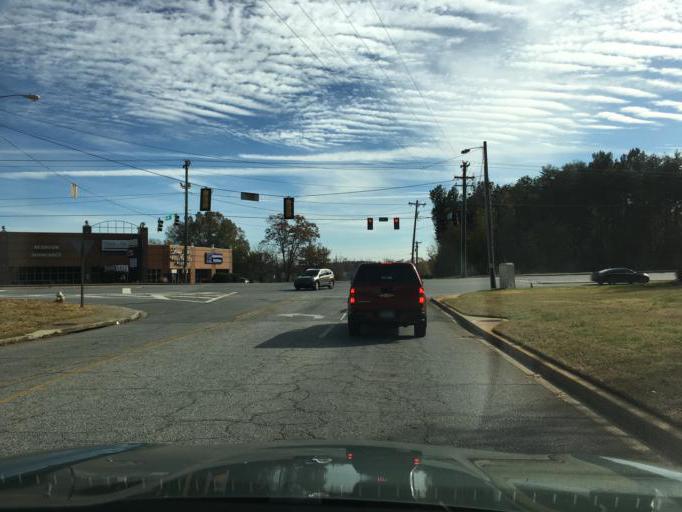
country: US
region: South Carolina
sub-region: Greenville County
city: Wade Hampton
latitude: 34.8427
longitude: -82.3301
